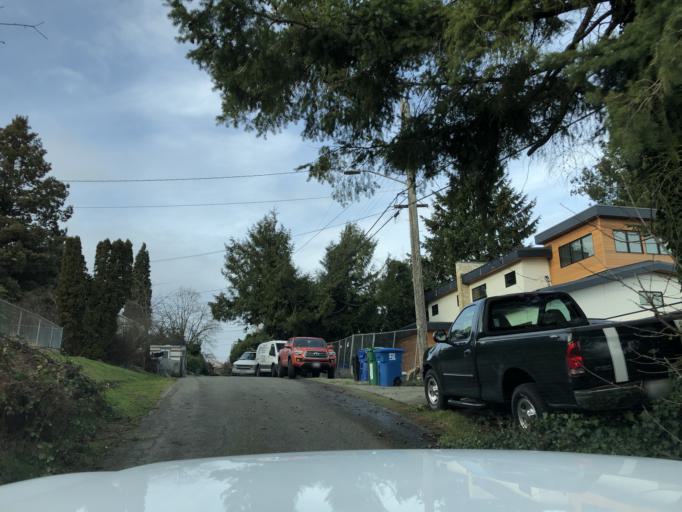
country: US
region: Washington
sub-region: King County
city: Lake Forest Park
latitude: 47.7137
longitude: -122.2798
